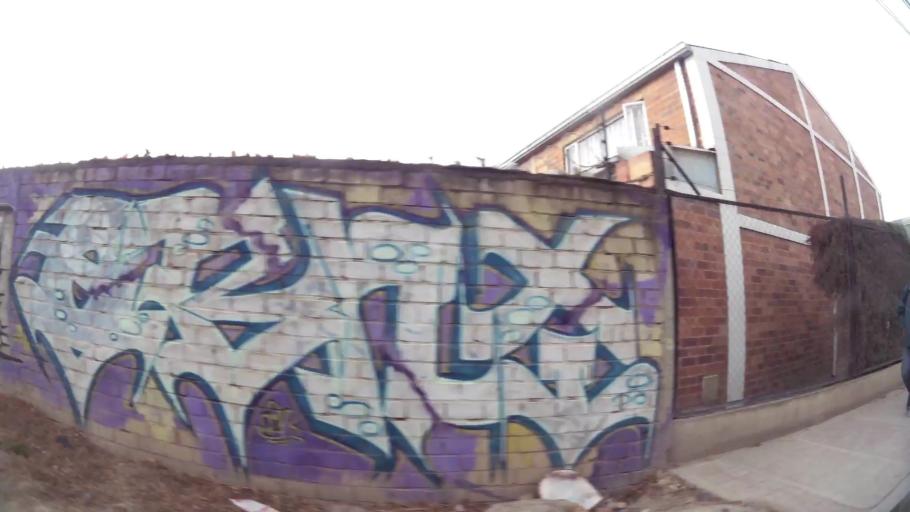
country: CO
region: Cundinamarca
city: Funza
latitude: 4.7053
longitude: -74.2126
